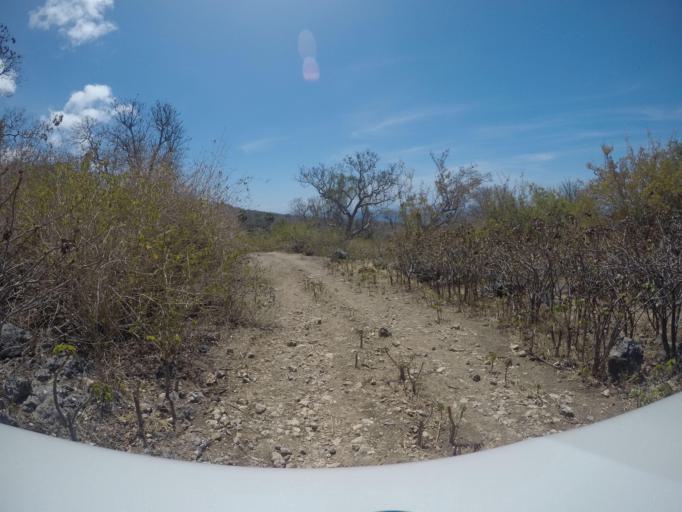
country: TL
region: Baucau
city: Baucau
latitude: -8.4399
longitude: 126.4407
